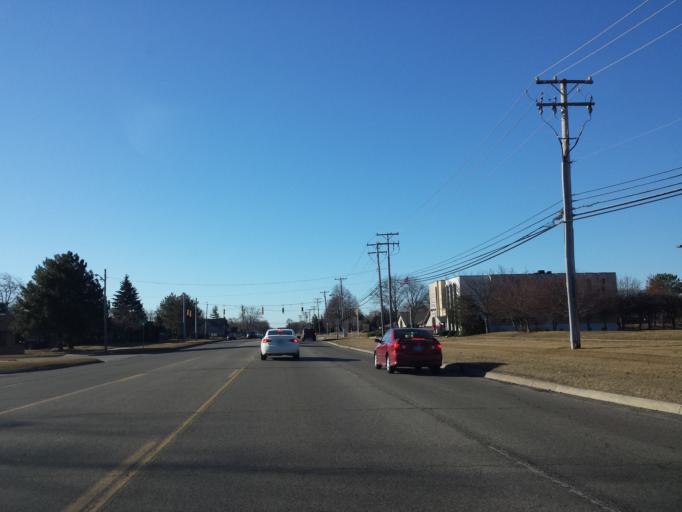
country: US
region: Michigan
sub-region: Oakland County
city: Clawson
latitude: 42.5575
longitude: -83.1475
